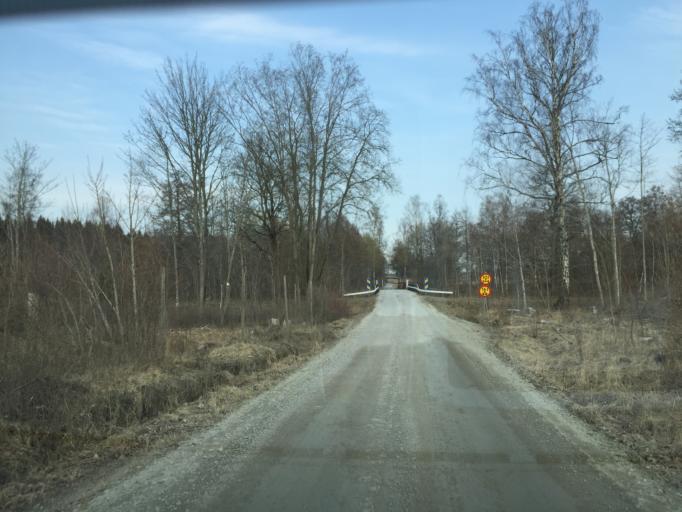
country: SE
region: Soedermanland
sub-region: Vingakers Kommun
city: Vingaker
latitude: 59.0406
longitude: 15.7854
